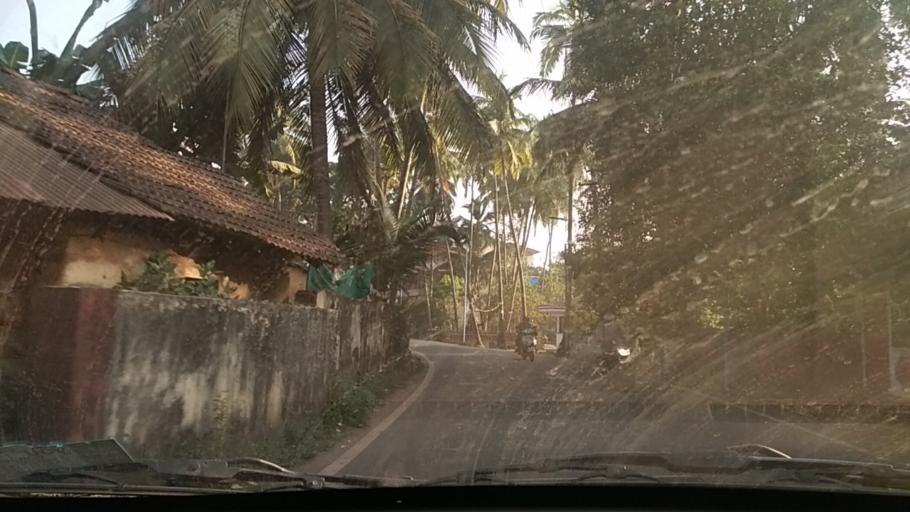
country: IN
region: Goa
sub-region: South Goa
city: Cuncolim
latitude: 15.1799
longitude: 73.9996
